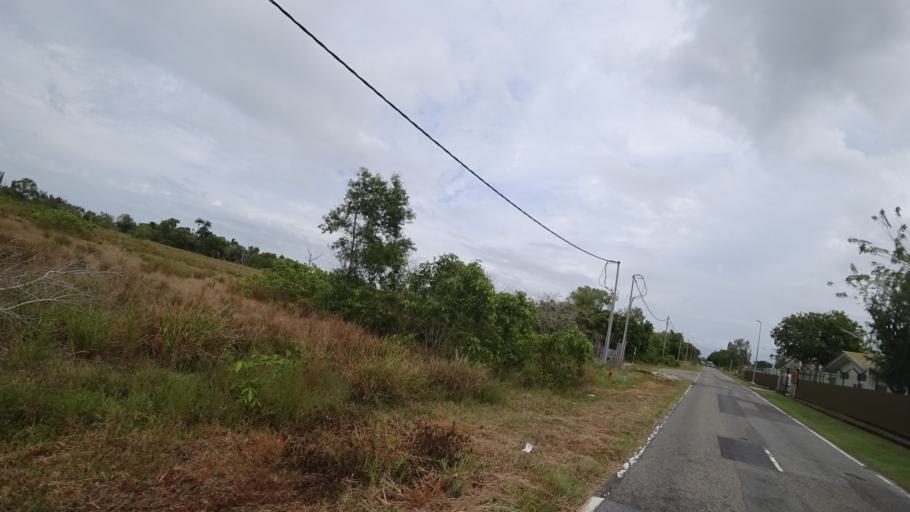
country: BN
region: Tutong
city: Tutong
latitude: 4.8076
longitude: 114.6410
